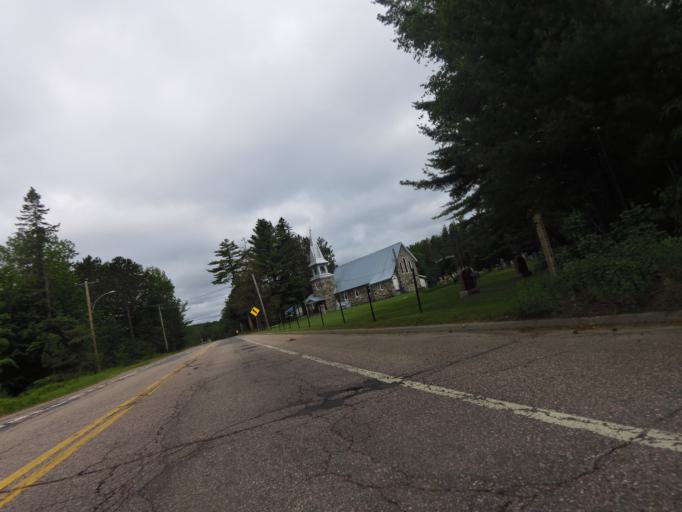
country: CA
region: Quebec
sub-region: Outaouais
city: Shawville
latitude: 45.8386
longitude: -76.4493
